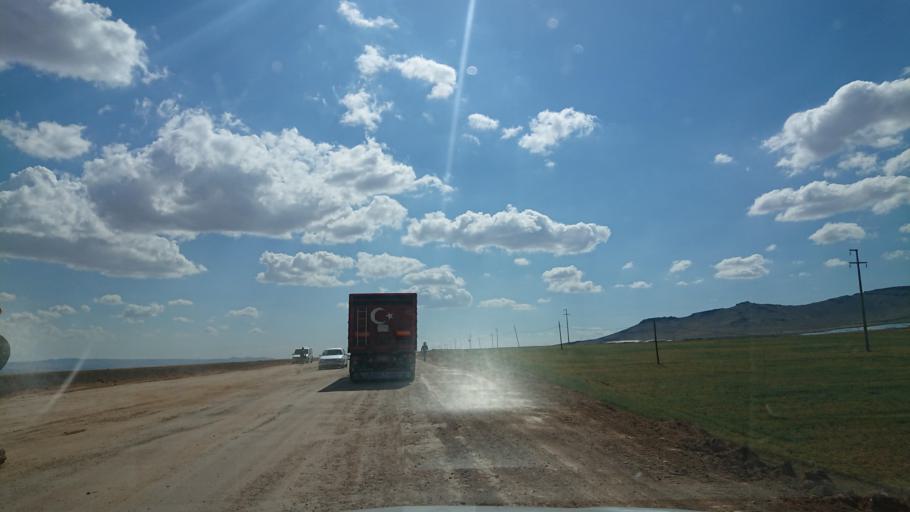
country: TR
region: Kirsehir
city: Kirsehir
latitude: 39.1402
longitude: 34.0677
